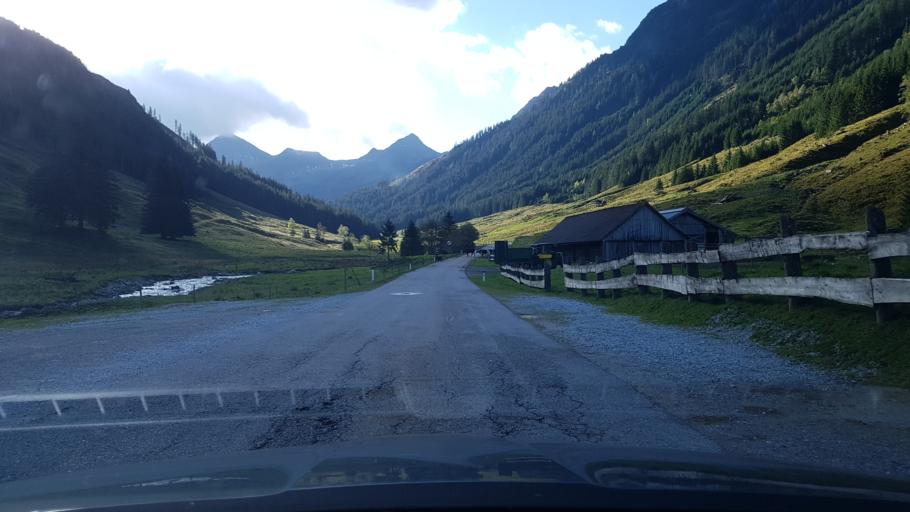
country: AT
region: Styria
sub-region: Politischer Bezirk Liezen
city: Sankt Nikolai im Solktal
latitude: 47.3110
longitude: 14.0590
